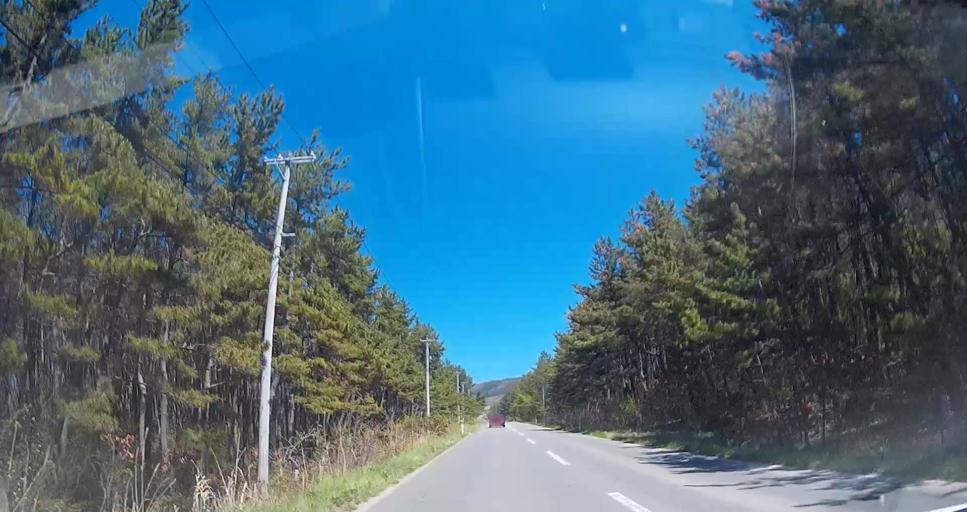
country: JP
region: Aomori
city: Mutsu
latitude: 41.3759
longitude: 141.3917
